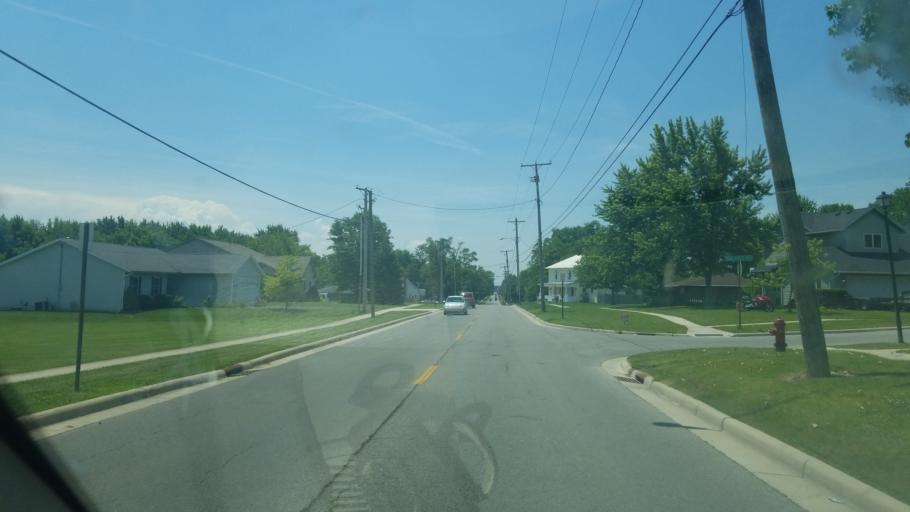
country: US
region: Ohio
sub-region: Hancock County
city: Findlay
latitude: 41.0642
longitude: -83.6330
